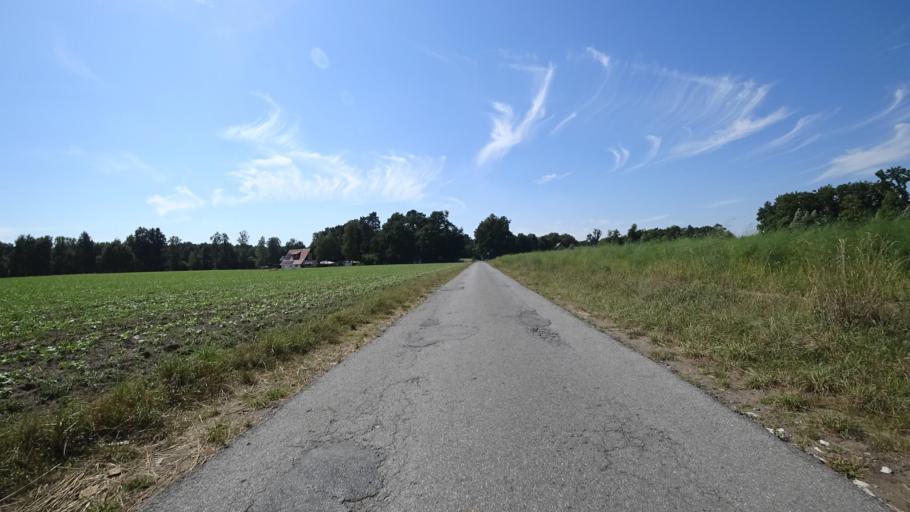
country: DE
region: North Rhine-Westphalia
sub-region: Regierungsbezirk Detmold
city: Verl
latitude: 51.9475
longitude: 8.4649
